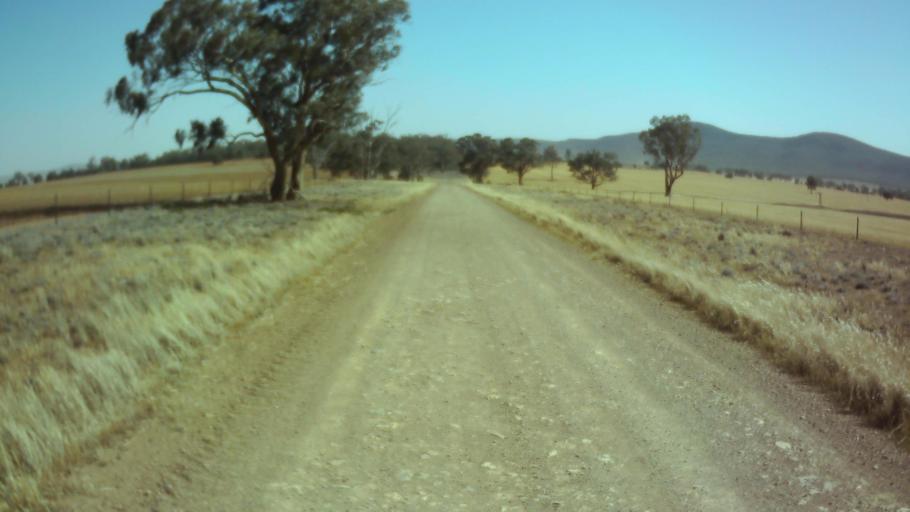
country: AU
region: New South Wales
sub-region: Weddin
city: Grenfell
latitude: -33.8528
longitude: 148.0161
